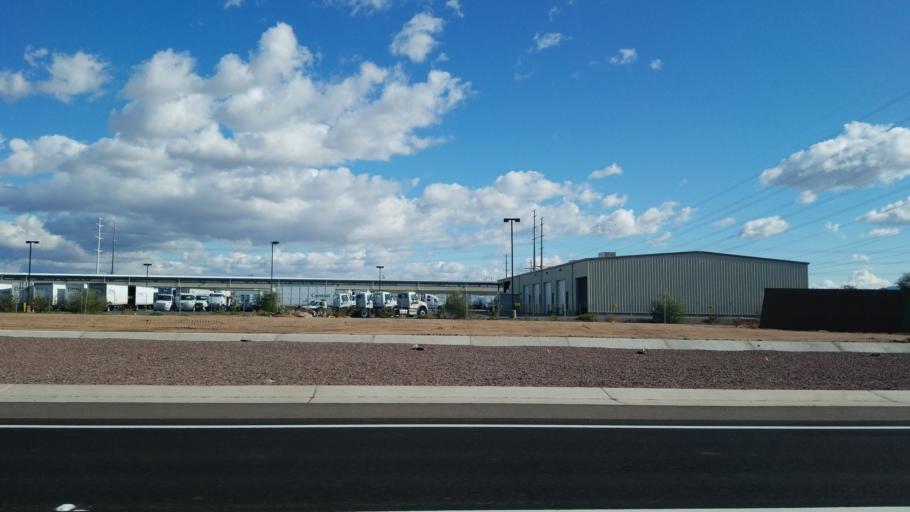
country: US
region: Arizona
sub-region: Maricopa County
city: Laveen
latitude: 33.4162
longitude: -112.1915
